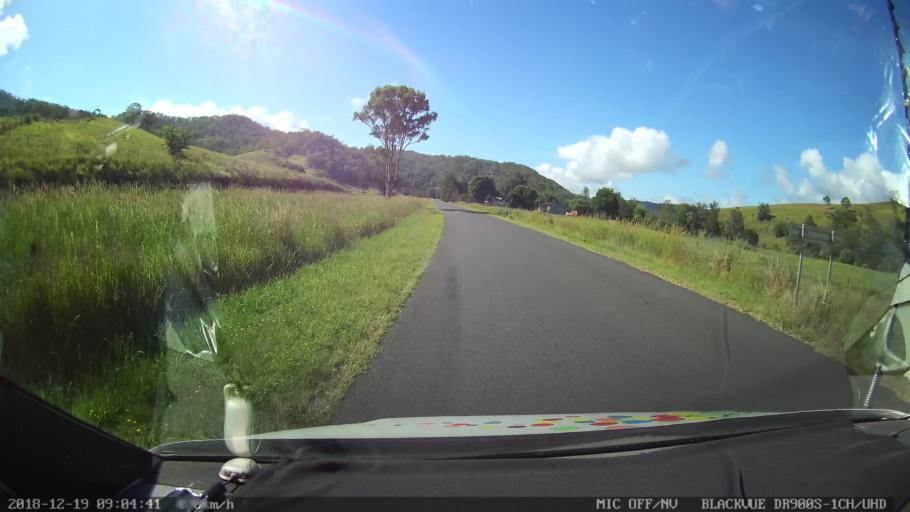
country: AU
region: New South Wales
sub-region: Kyogle
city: Kyogle
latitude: -28.4569
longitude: 152.9442
